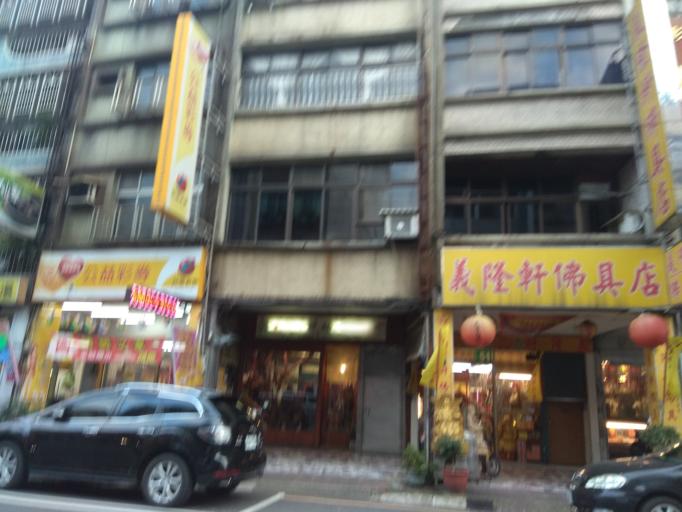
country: TW
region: Taiwan
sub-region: Taoyuan
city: Taoyuan
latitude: 24.9949
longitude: 121.3117
